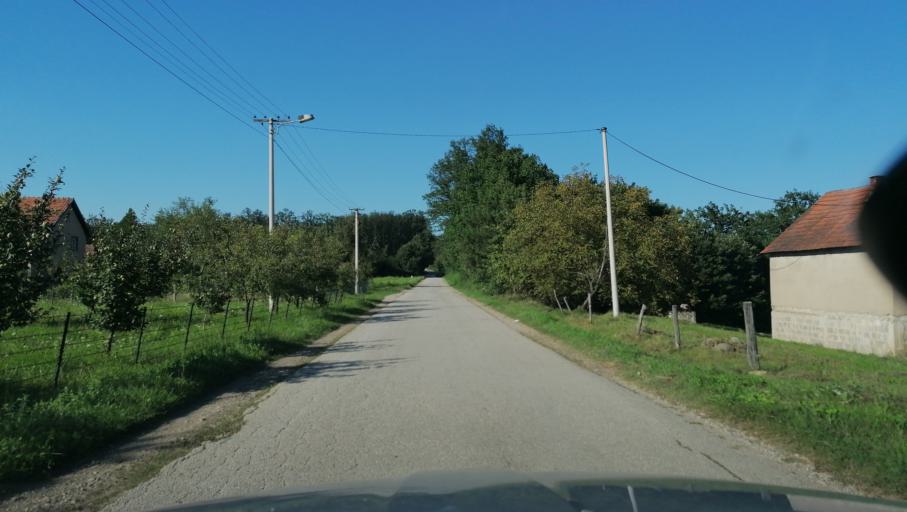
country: RS
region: Central Serbia
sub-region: Sumadijski Okrug
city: Knic
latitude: 43.8820
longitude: 20.6137
